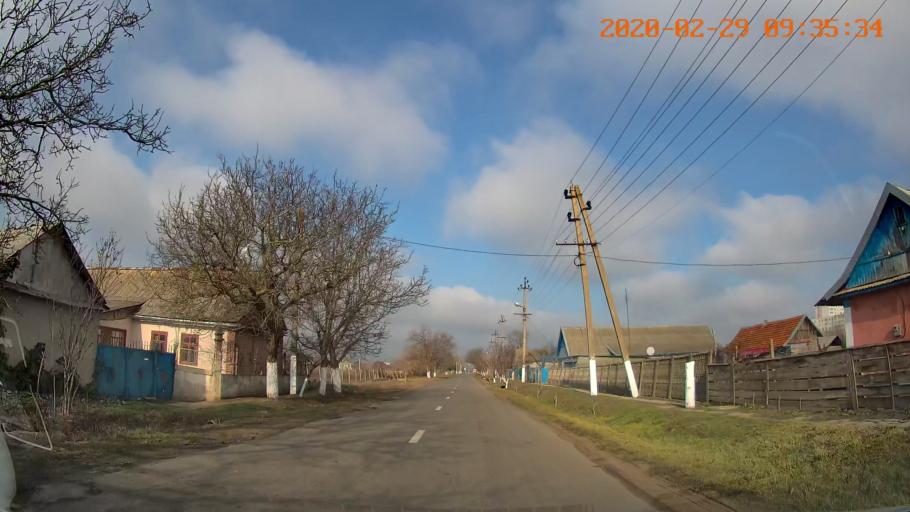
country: MD
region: Telenesti
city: Dnestrovsc
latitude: 46.6197
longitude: 29.8981
